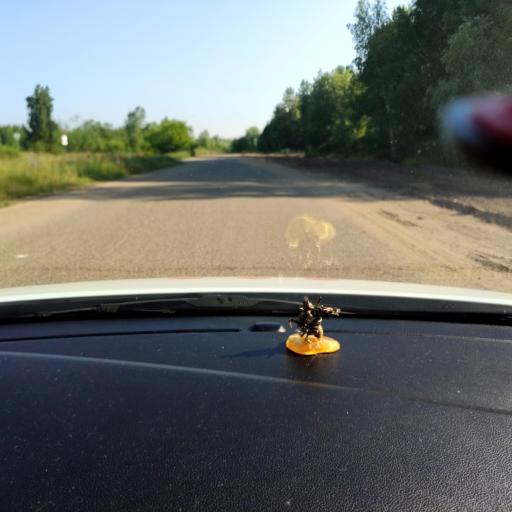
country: RU
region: Tatarstan
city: Stolbishchi
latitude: 55.6977
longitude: 49.2228
